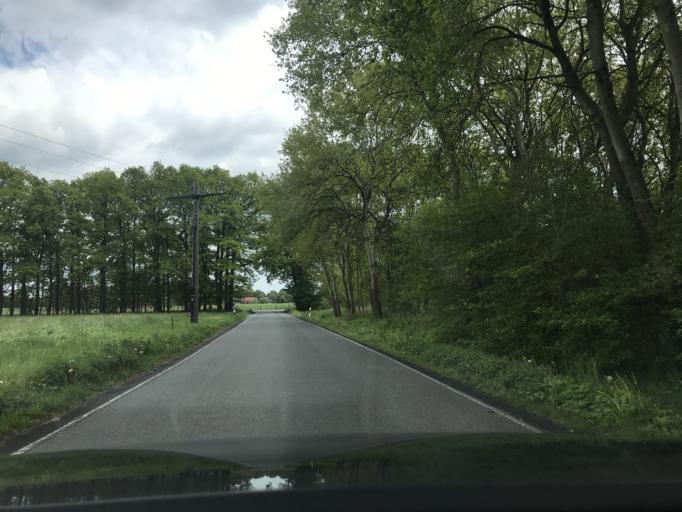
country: DE
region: North Rhine-Westphalia
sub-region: Regierungsbezirk Detmold
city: Harsewinkel
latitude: 51.9000
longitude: 8.2432
